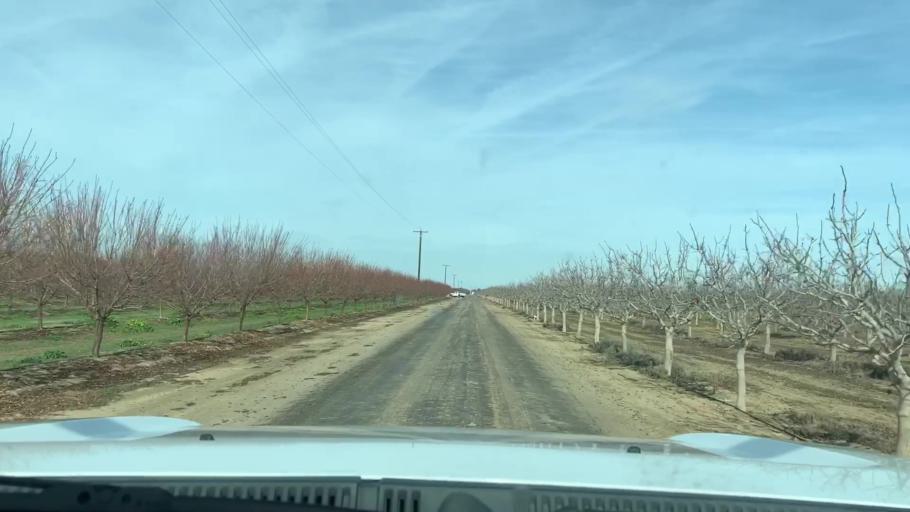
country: US
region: California
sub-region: Kern County
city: Lost Hills
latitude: 35.6061
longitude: -119.5357
